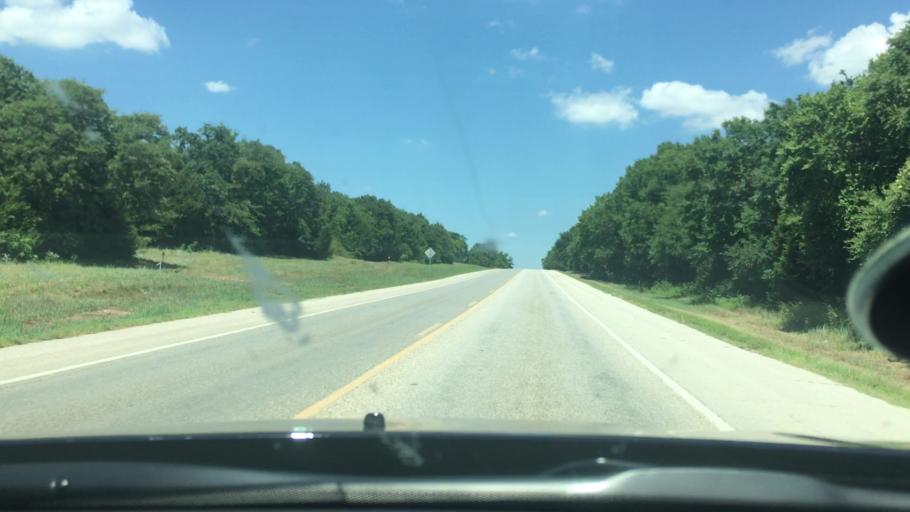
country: US
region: Oklahoma
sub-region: Marshall County
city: Oakland
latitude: 34.1768
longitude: -96.8599
